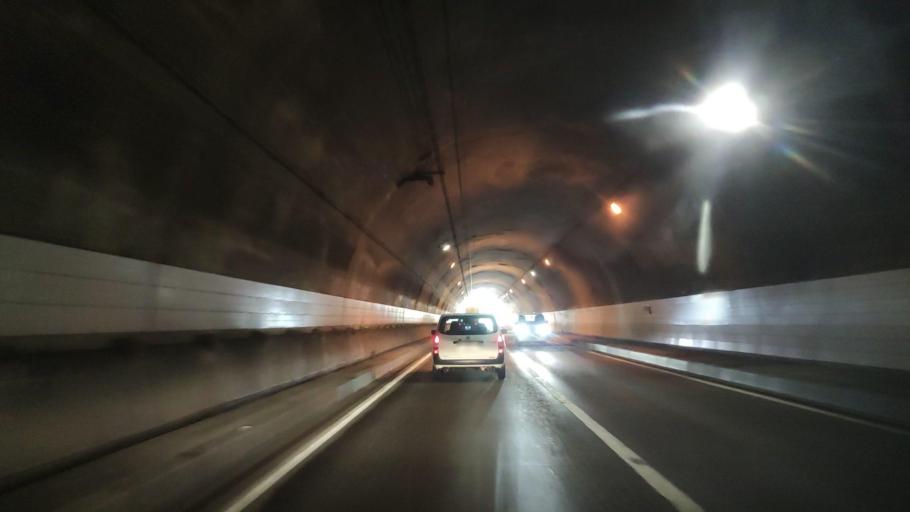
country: JP
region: Toyama
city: Yatsuomachi-higashikumisaka
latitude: 36.4522
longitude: 137.2578
